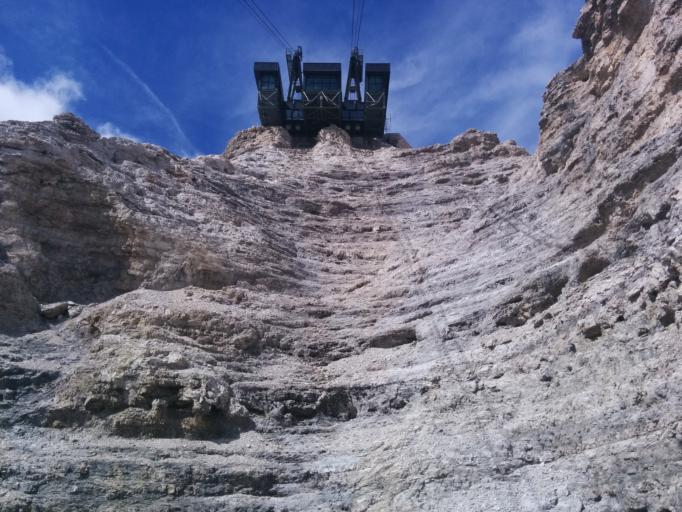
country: IT
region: Trentino-Alto Adige
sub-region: Provincia di Trento
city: Canazei
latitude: 46.4997
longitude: 11.8081
